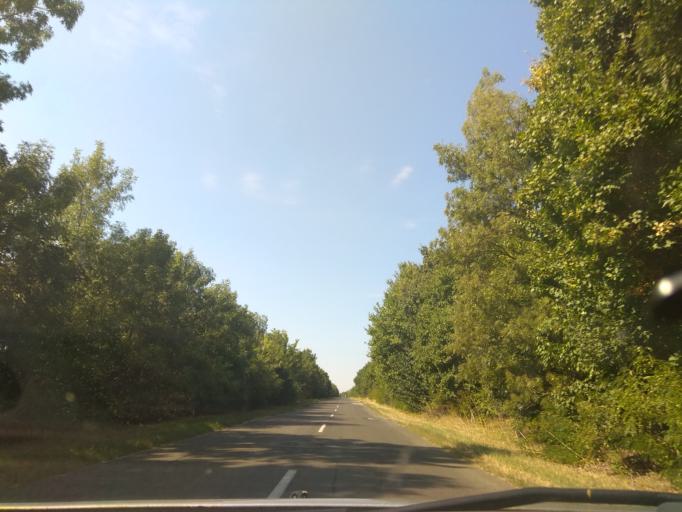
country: HU
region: Borsod-Abauj-Zemplen
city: Harsany
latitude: 47.9350
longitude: 20.7352
